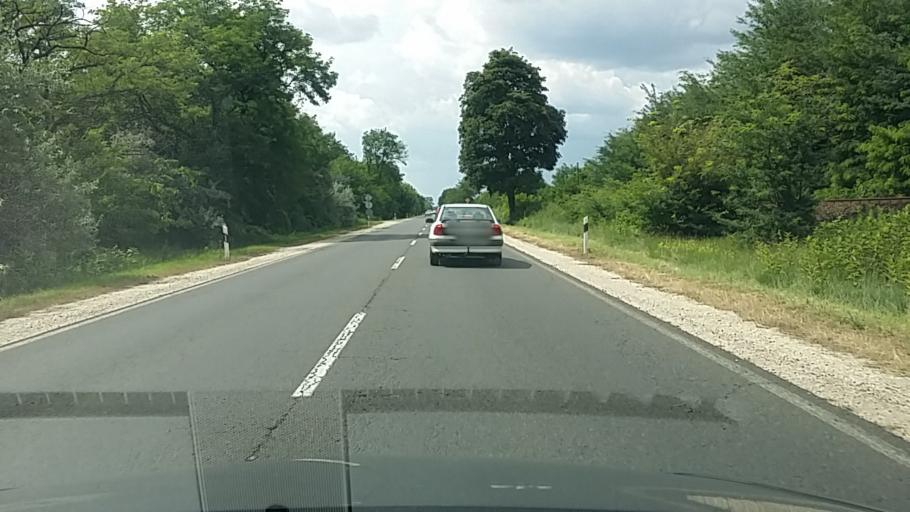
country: HU
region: Pest
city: Ujhartyan
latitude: 47.1736
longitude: 19.3633
